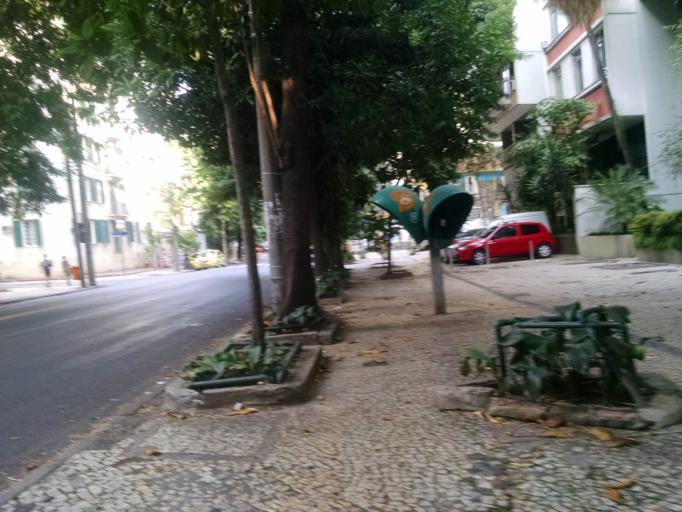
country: BR
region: Rio de Janeiro
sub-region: Rio De Janeiro
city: Rio de Janeiro
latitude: -22.9383
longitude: -43.1952
